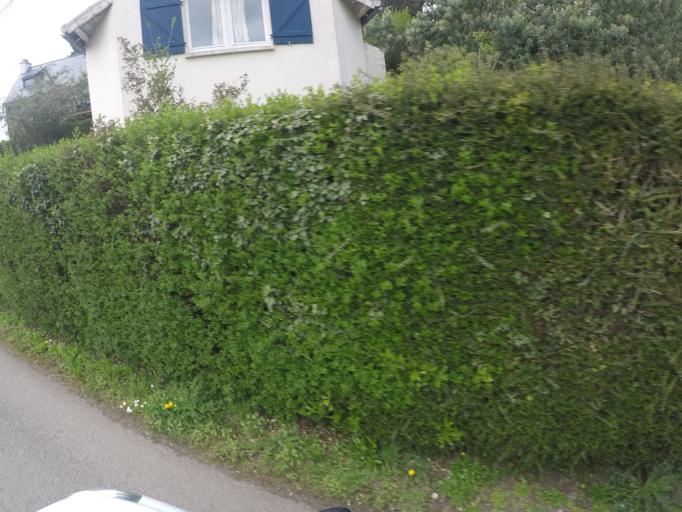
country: FR
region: Brittany
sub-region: Departement des Cotes-d'Armor
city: Plouezec
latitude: 48.7225
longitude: -2.9513
